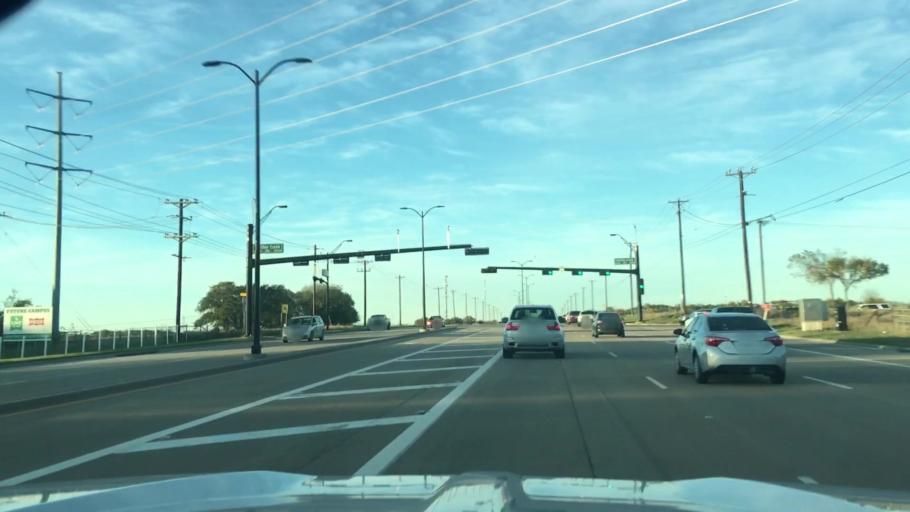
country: US
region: Texas
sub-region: Collin County
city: Frisco
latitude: 33.1888
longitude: -96.8028
